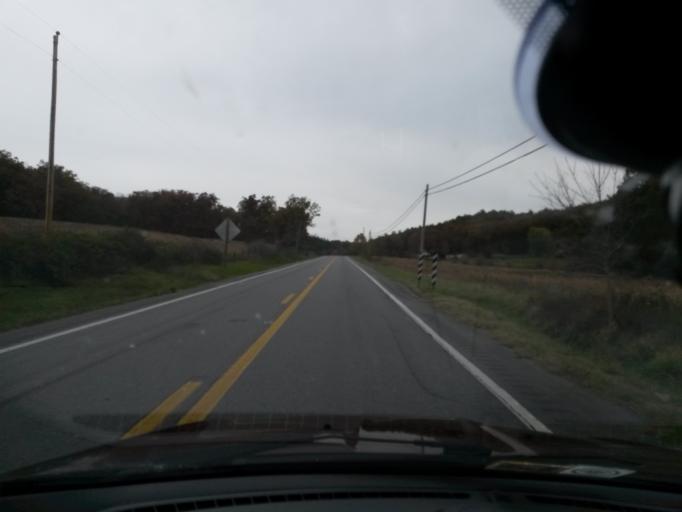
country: US
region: Virginia
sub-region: Alleghany County
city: Clifton Forge
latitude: 37.7495
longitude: -79.7895
